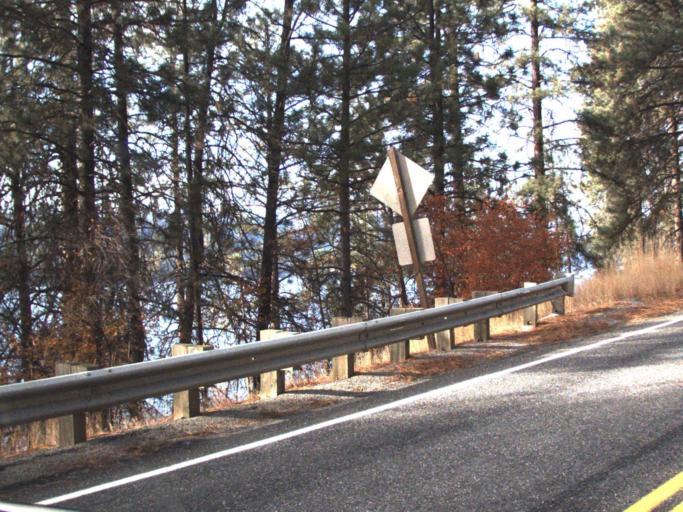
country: US
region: Washington
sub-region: Stevens County
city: Kettle Falls
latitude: 48.3638
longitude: -118.1634
